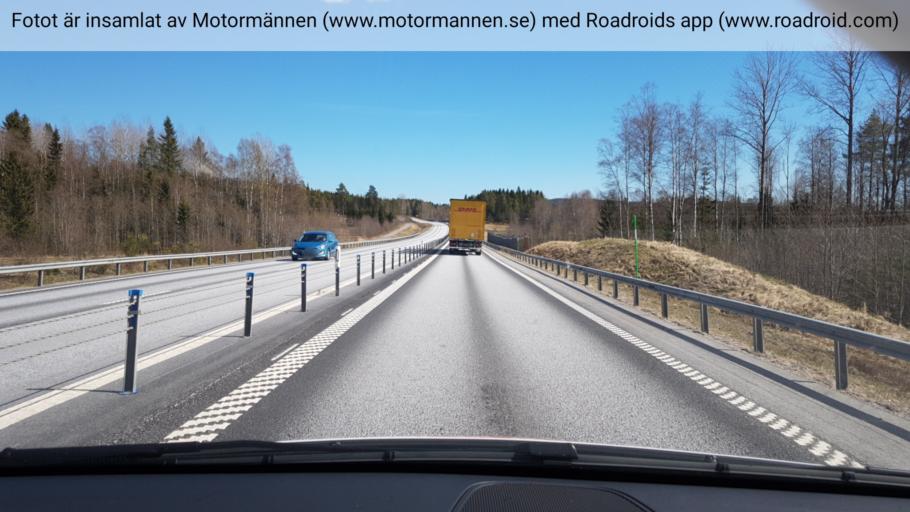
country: SE
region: Vaesterbotten
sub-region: Vannas Kommun
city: Vannasby
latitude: 63.8981
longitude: 19.9108
